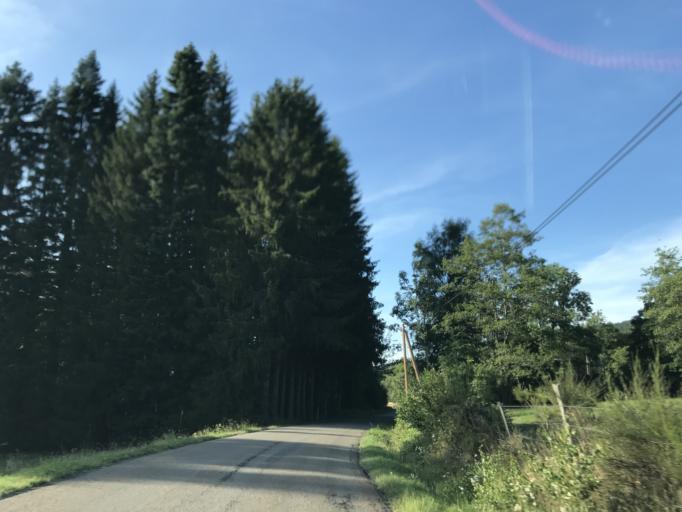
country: FR
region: Auvergne
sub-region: Departement du Puy-de-Dome
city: Job
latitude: 45.6859
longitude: 3.7322
